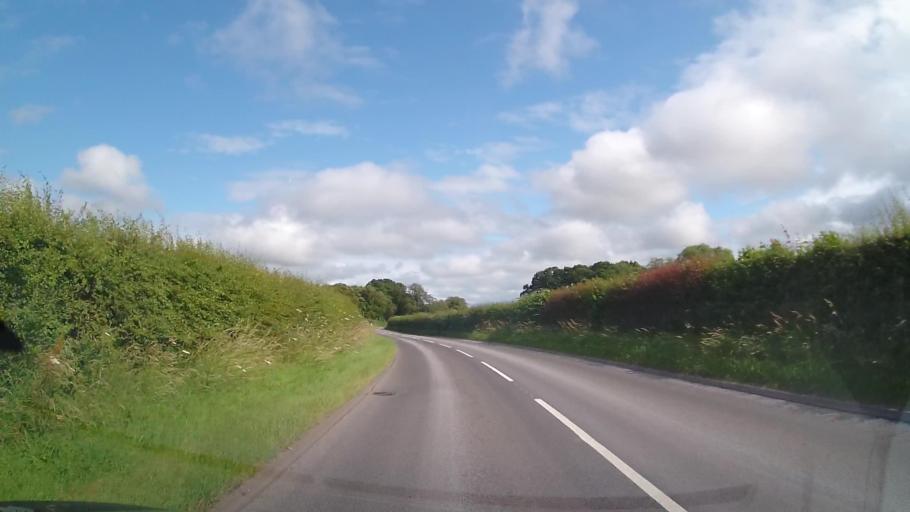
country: GB
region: England
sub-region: Shropshire
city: Pant
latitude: 52.8087
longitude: -3.0321
